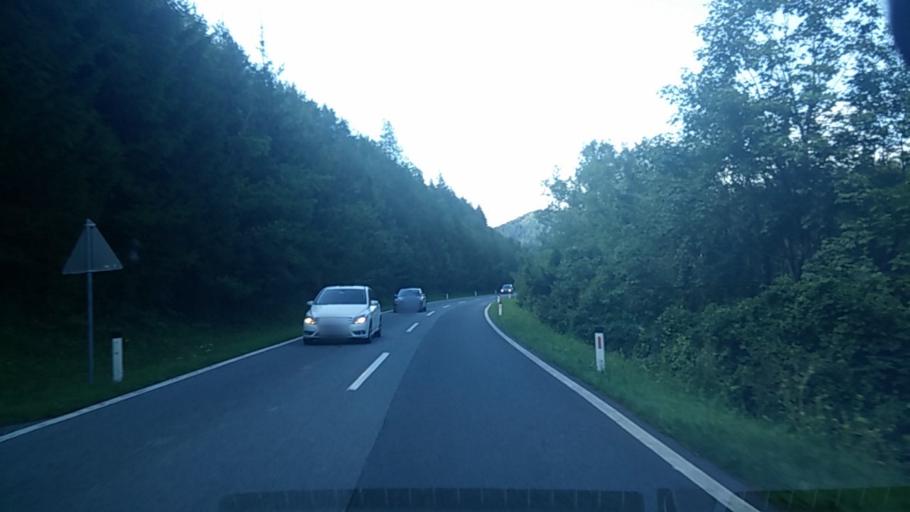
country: AT
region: Carinthia
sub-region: Politischer Bezirk Volkermarkt
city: Sittersdorf
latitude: 46.5330
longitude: 14.5936
